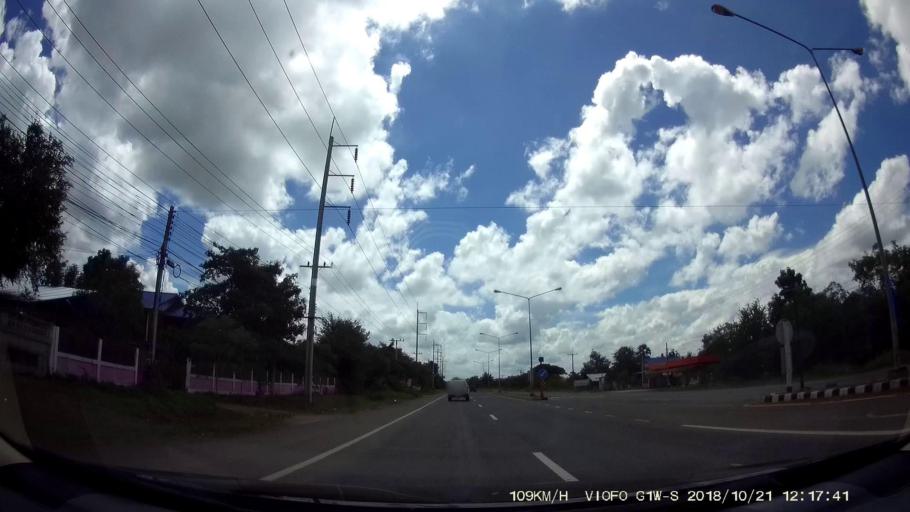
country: TH
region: Nakhon Ratchasima
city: Dan Khun Thot
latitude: 15.3281
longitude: 101.8191
